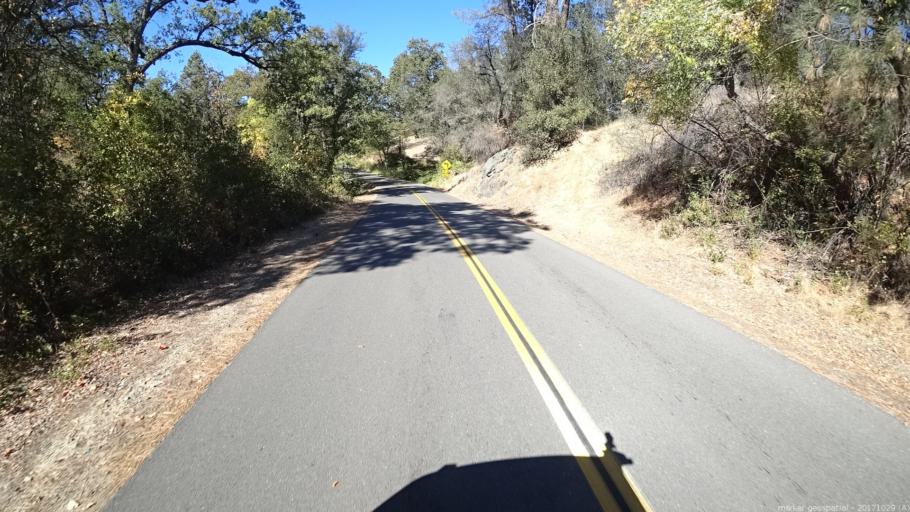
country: US
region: California
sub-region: Shasta County
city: Shasta
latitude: 40.4817
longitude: -122.6315
